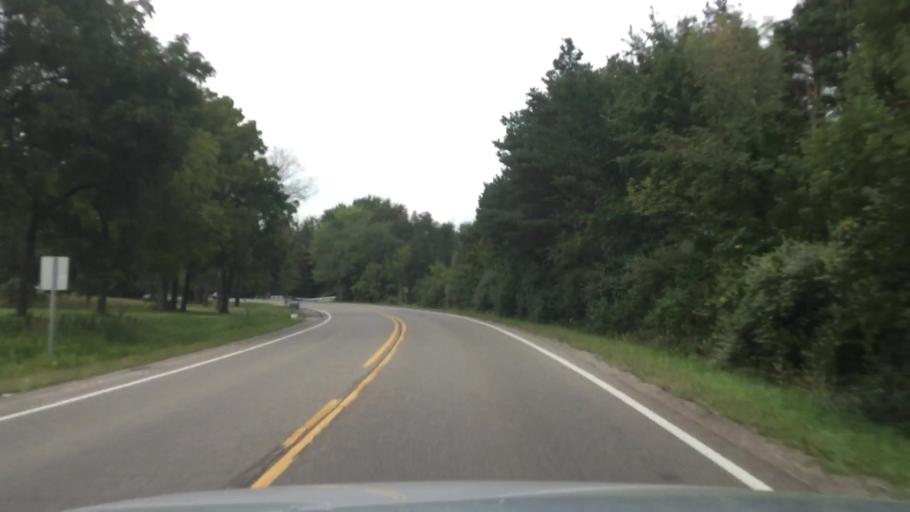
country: US
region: Michigan
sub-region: Genesee County
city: Linden
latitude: 42.8635
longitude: -83.7698
